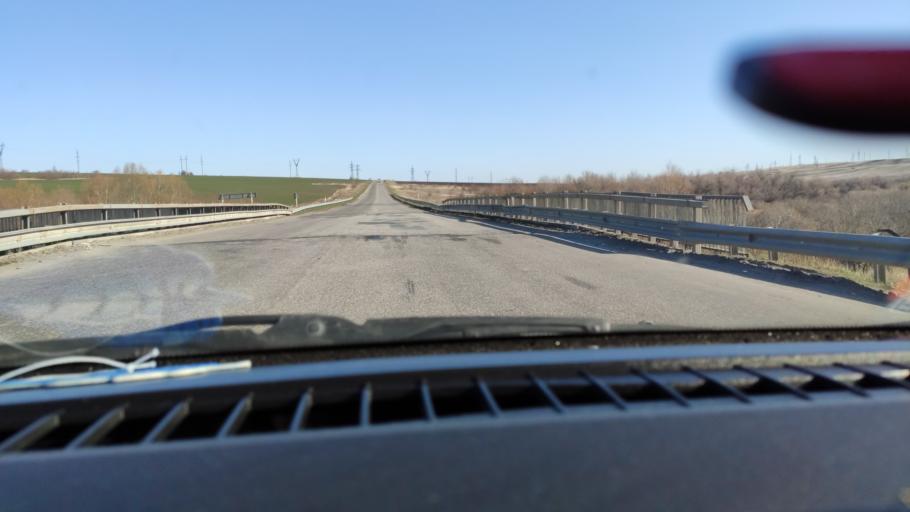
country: RU
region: Samara
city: Varlamovo
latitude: 53.0718
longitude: 48.3540
